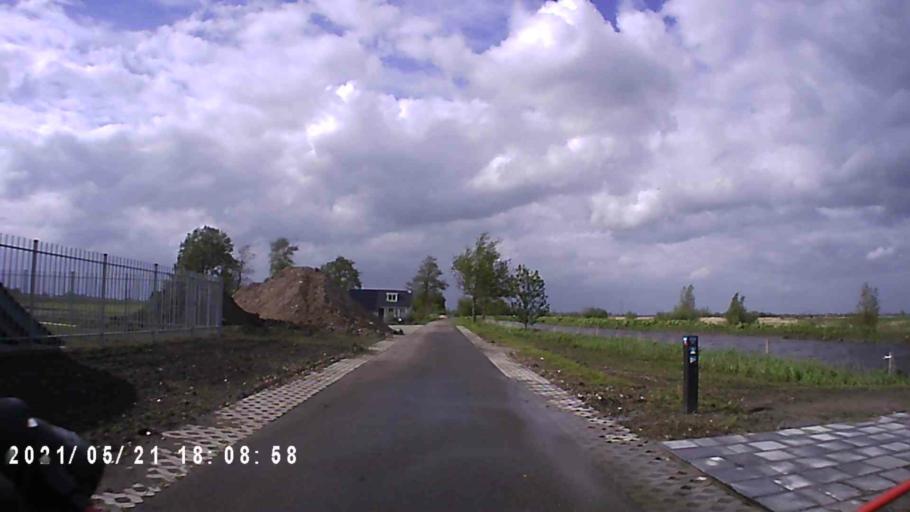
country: NL
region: Groningen
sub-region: Gemeente Zuidhorn
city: Zuidhorn
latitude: 53.1973
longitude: 6.4145
